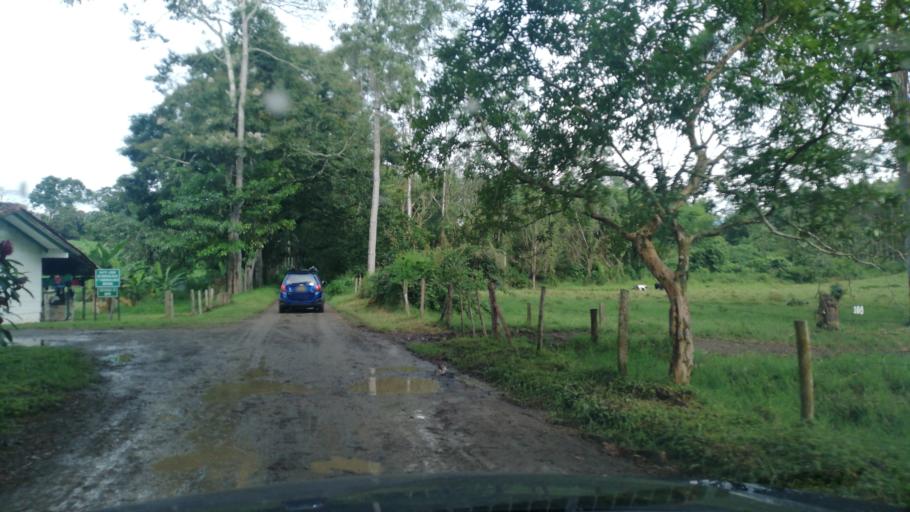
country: CO
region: Valle del Cauca
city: Restrepo
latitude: 3.8530
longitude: -76.4643
